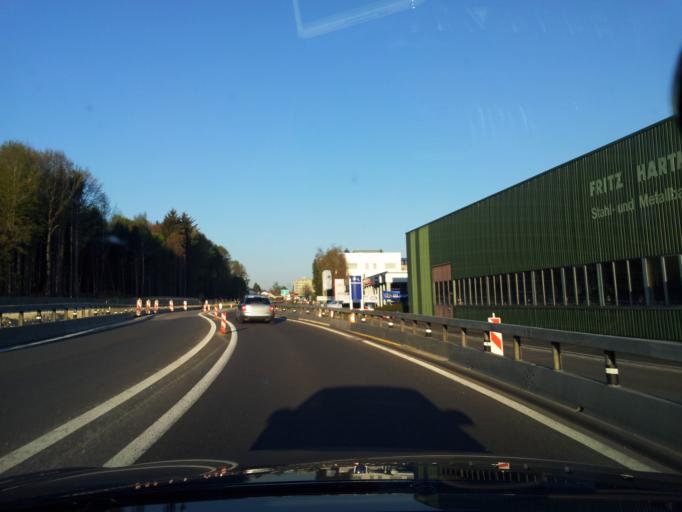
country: CH
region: Bern
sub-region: Biel/Bienne District
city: Brugg
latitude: 47.1213
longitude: 7.2682
